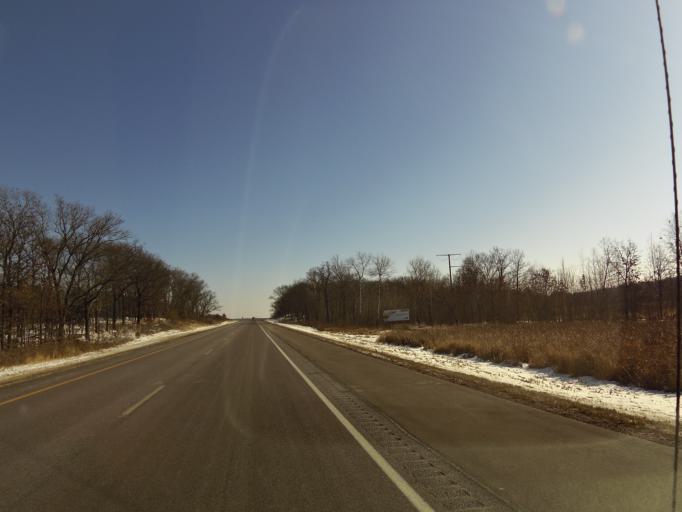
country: US
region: Wisconsin
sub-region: Juneau County
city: Mauston
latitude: 43.7427
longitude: -89.9381
